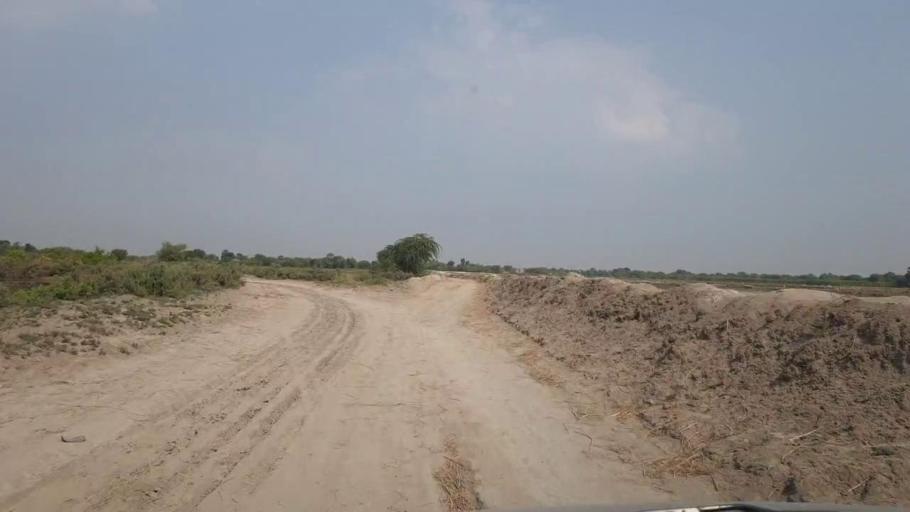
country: PK
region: Sindh
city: Matli
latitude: 24.9706
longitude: 68.6952
